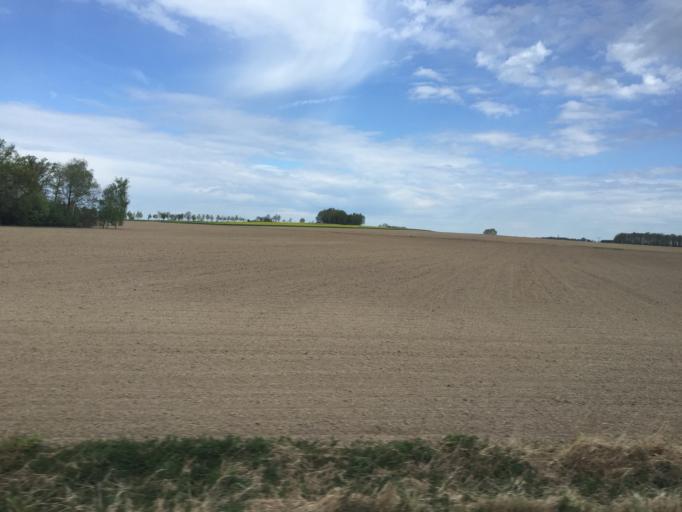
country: DE
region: Saxony
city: Obergurig
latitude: 51.1674
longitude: 14.3720
